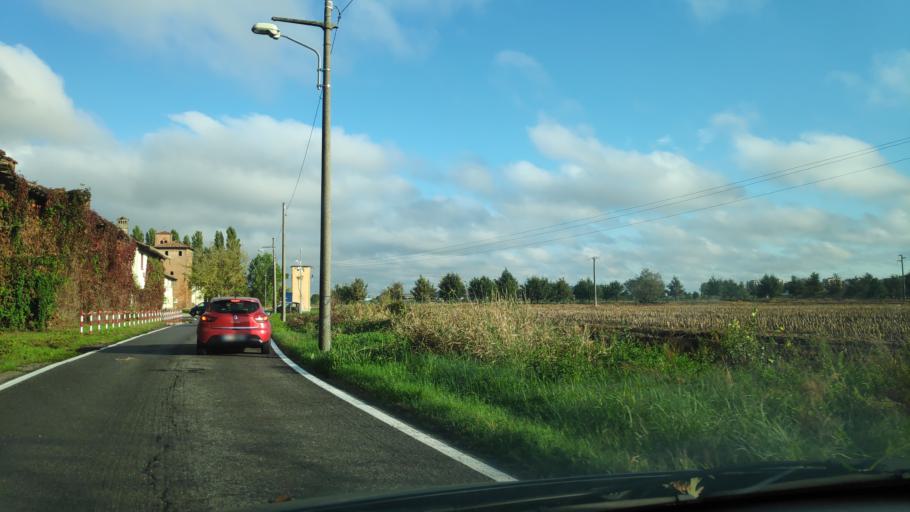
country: IT
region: Lombardy
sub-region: Citta metropolitana di Milano
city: Noverasco-Sporting Mirasole
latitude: 45.3863
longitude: 9.2032
